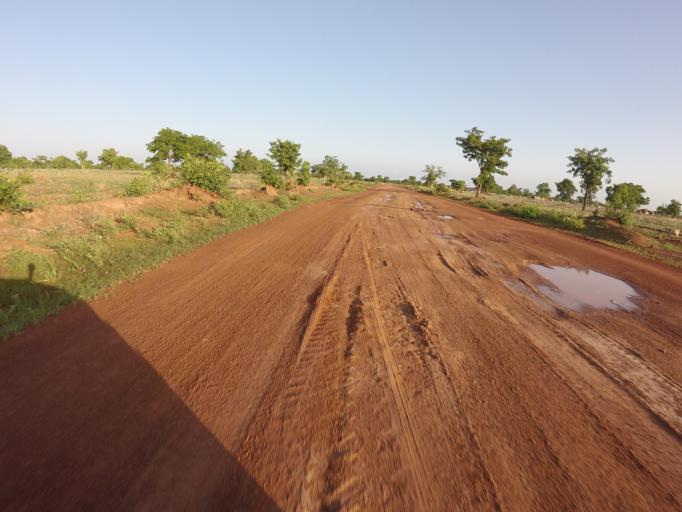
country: TG
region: Savanes
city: Sansanne-Mango
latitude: 10.2932
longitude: -0.0876
